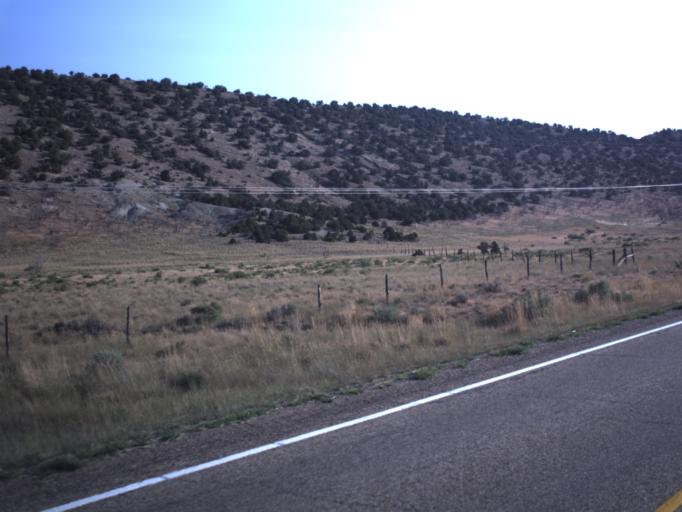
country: US
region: Utah
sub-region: Uintah County
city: Vernal
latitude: 40.5656
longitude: -109.5008
